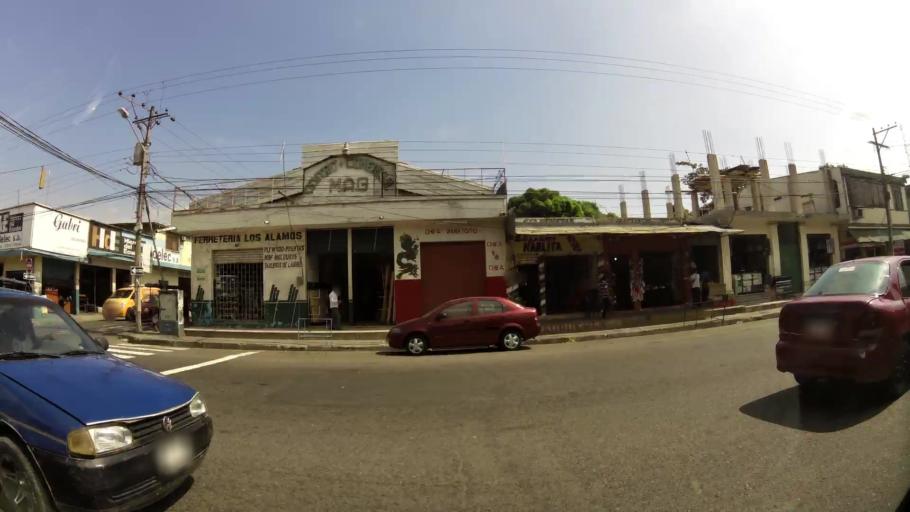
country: EC
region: Guayas
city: Eloy Alfaro
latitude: -2.1644
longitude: -79.8443
